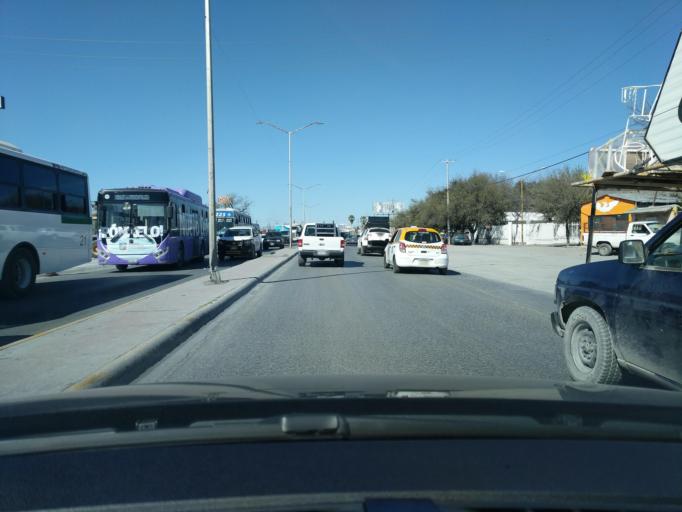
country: MX
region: Nuevo Leon
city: Juarez
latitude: 25.6429
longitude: -100.0879
